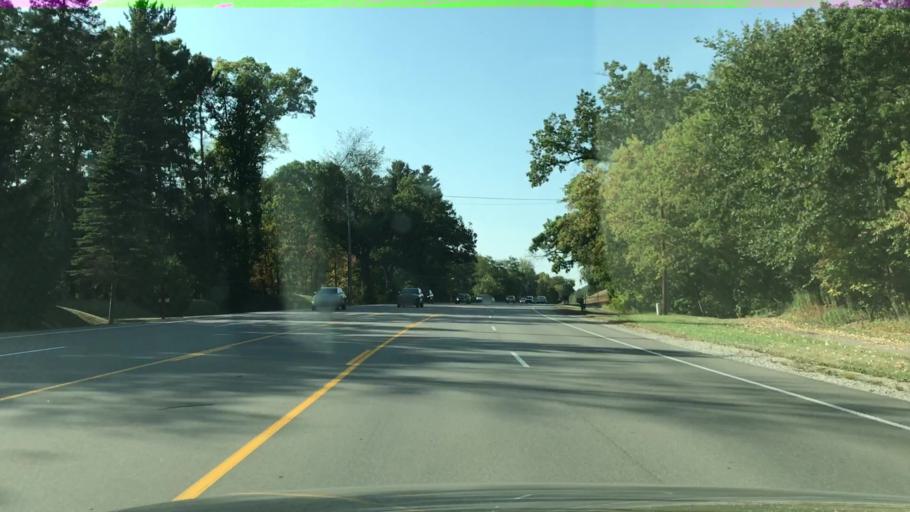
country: US
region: Michigan
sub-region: Kent County
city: Forest Hills
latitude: 42.9294
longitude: -85.5194
